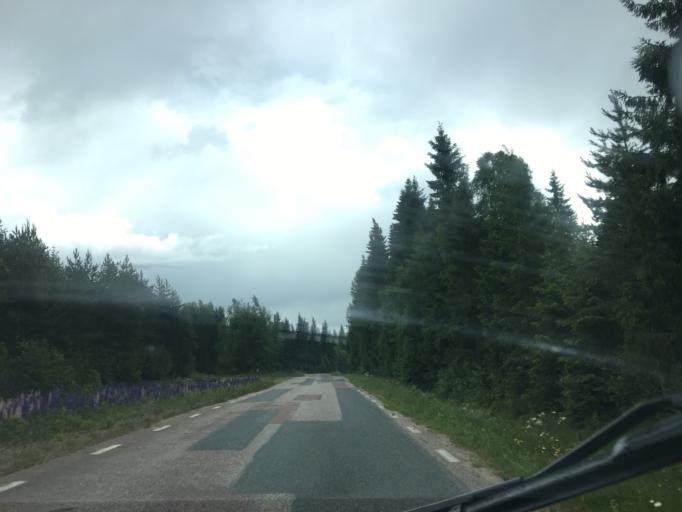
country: SE
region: OErebro
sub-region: Hallefors Kommun
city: Haellefors
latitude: 60.0556
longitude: 14.4975
